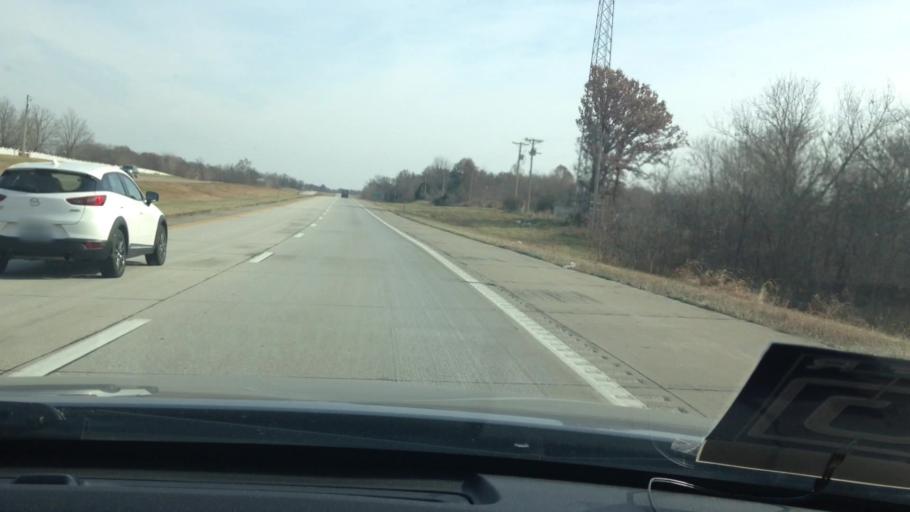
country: US
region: Missouri
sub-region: Cass County
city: Garden City
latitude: 38.4640
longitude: -93.9936
